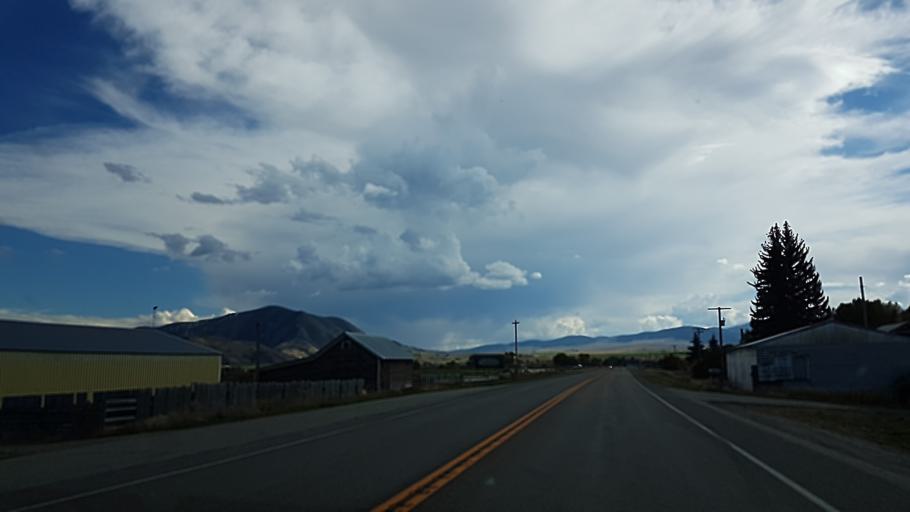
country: US
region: Montana
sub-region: Jefferson County
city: Whitehall
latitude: 45.8676
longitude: -111.9541
